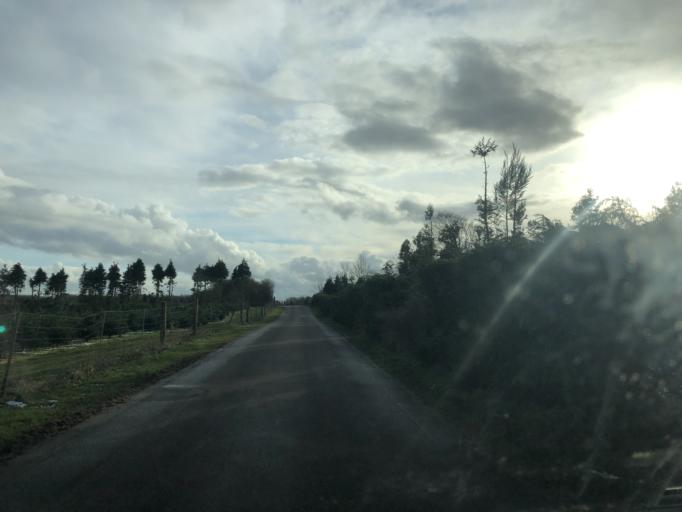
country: DK
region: Central Jutland
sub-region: Viborg Kommune
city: Viborg
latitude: 56.5089
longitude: 9.4268
